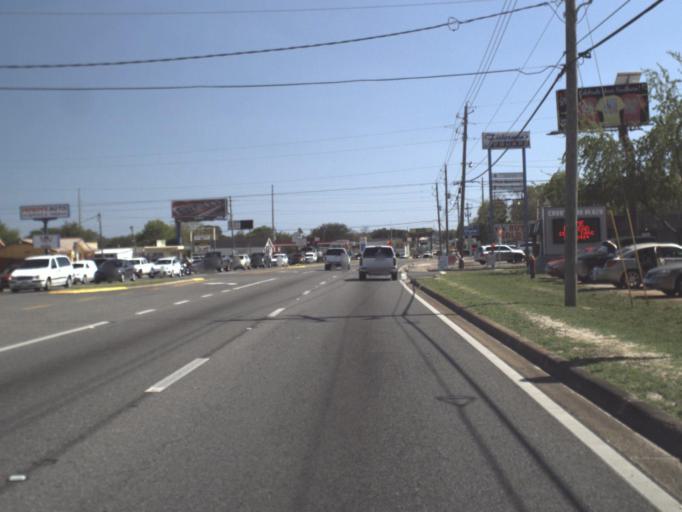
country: US
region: Florida
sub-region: Okaloosa County
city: Wright
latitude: 30.4377
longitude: -86.6389
